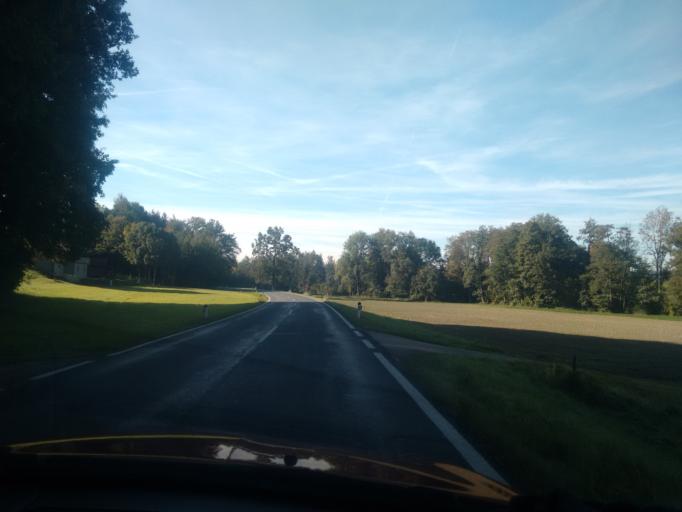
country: AT
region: Upper Austria
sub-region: Politischer Bezirk Vocklabruck
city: Manning
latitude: 48.0793
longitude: 13.6649
